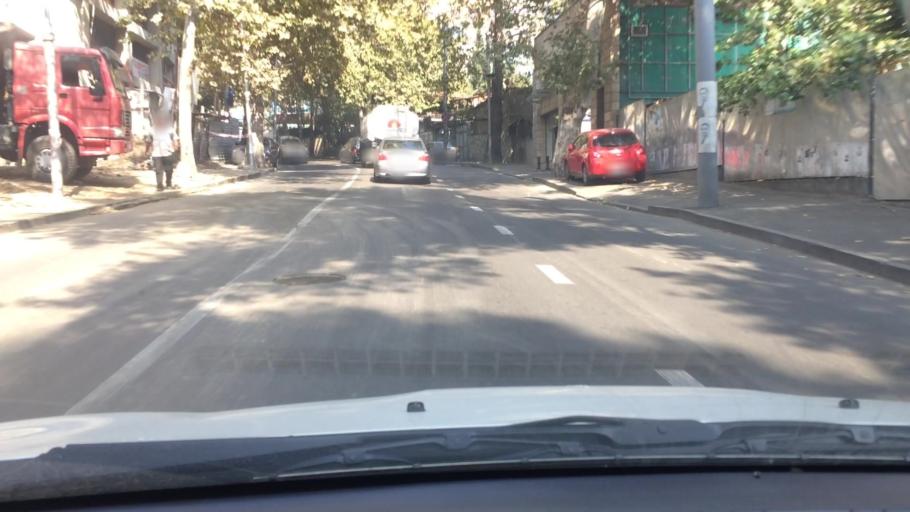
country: GE
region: T'bilisi
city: Tbilisi
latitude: 41.6857
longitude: 44.8260
